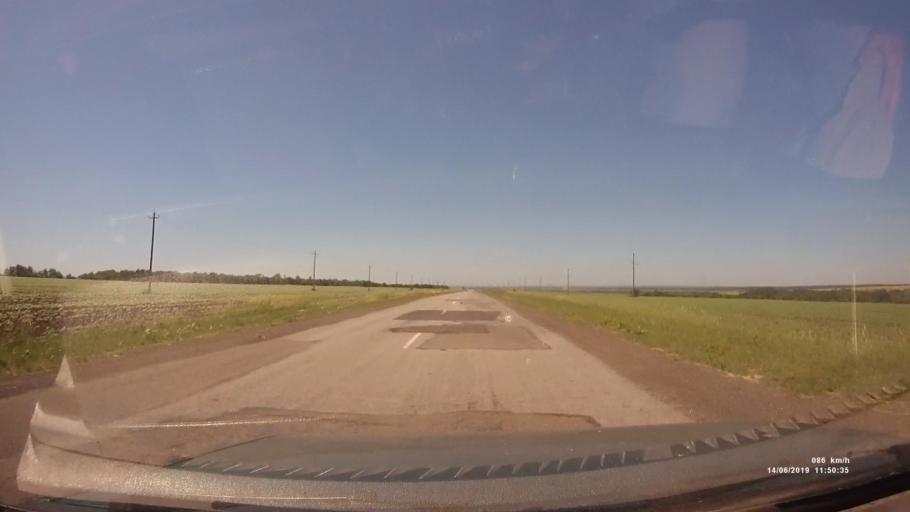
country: RU
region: Rostov
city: Kazanskaya
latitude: 49.8452
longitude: 41.2626
